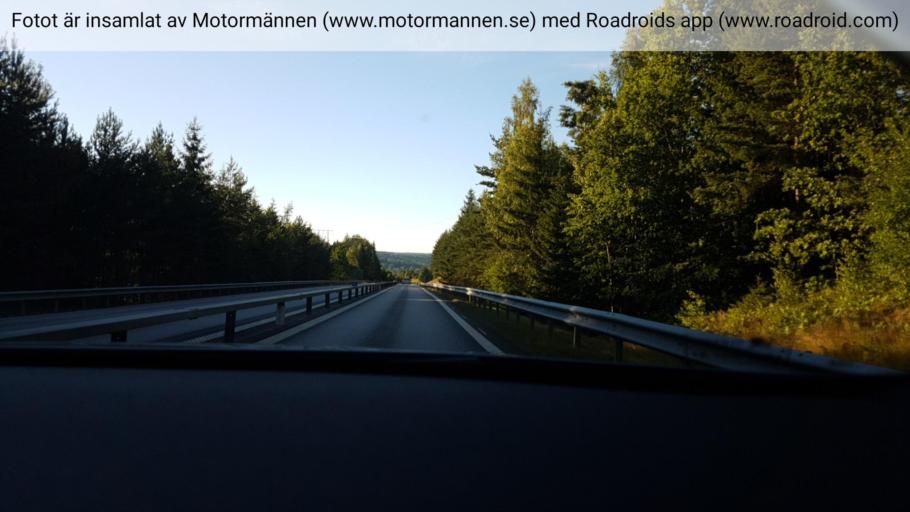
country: SE
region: Joenkoeping
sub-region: Jonkopings Kommun
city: Jonkoping
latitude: 57.7945
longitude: 14.0998
